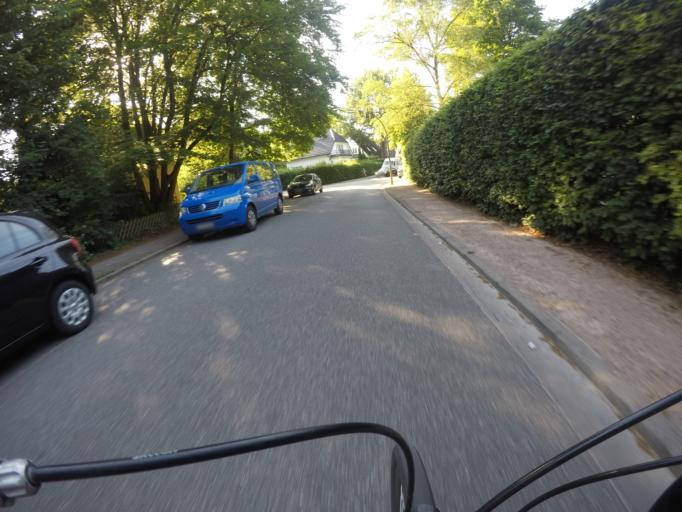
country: DE
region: Schleswig-Holstein
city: Halstenbek
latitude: 53.5712
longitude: 9.8188
